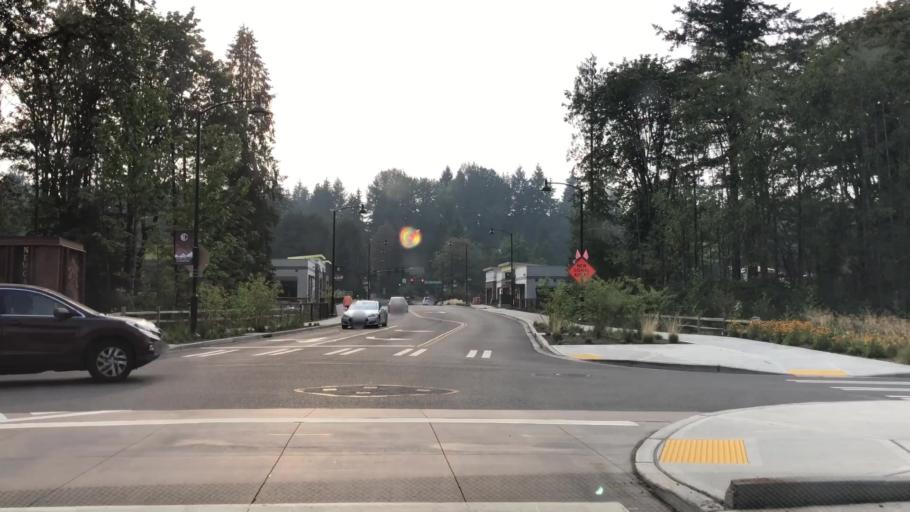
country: US
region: Washington
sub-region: King County
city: Newcastle
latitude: 47.5436
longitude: -122.1617
